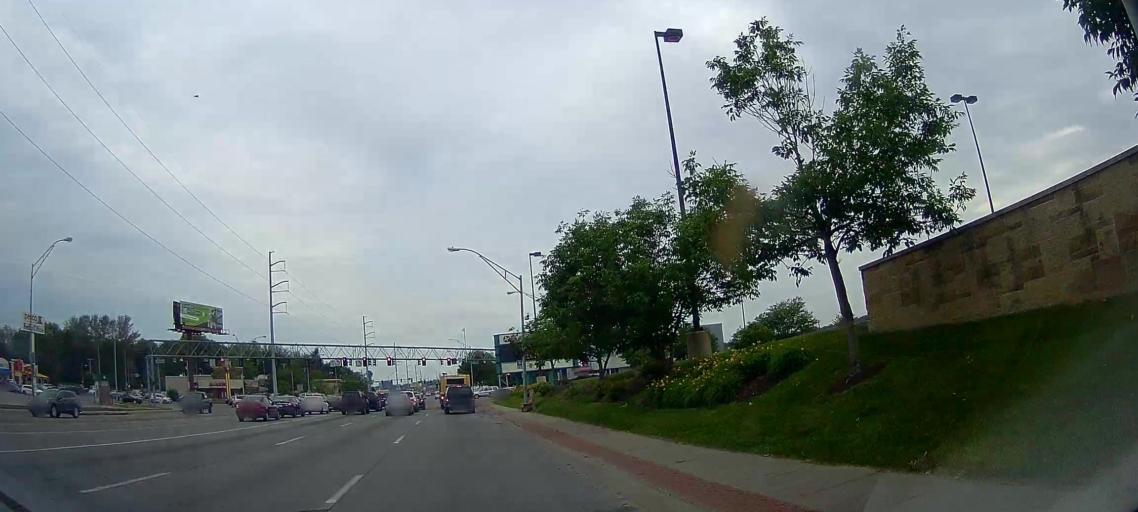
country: US
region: Nebraska
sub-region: Douglas County
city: Ralston
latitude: 41.2605
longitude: -96.0240
